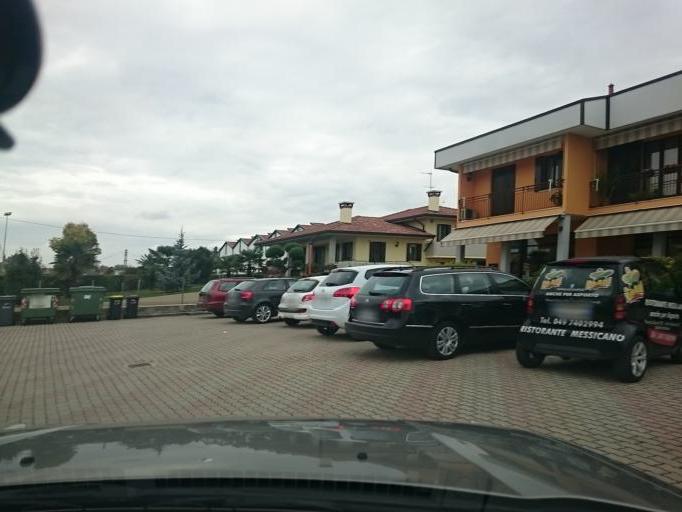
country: IT
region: Veneto
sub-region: Provincia di Padova
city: Arzergrande
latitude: 45.2707
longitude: 12.0282
